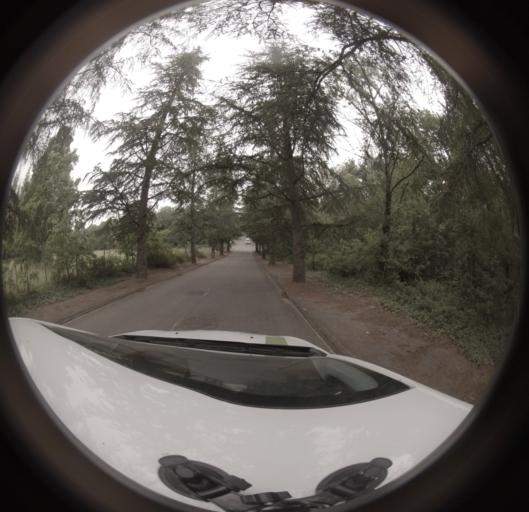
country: FR
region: Midi-Pyrenees
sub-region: Departement du Tarn-et-Garonne
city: Montauban
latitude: 44.0074
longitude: 1.3927
